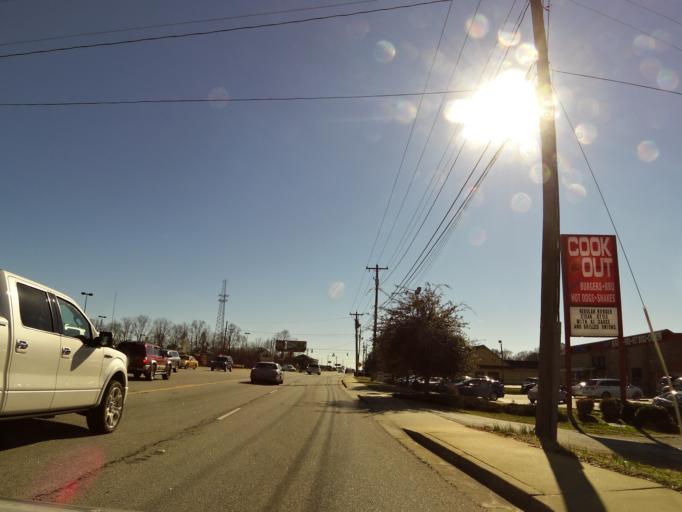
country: US
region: South Carolina
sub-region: Greenville County
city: Sans Souci
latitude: 34.8893
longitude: -82.4057
